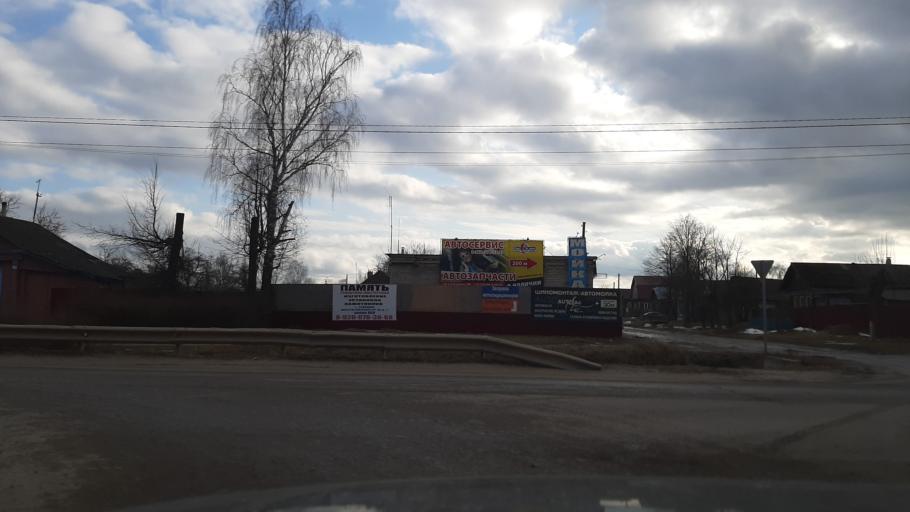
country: RU
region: Ivanovo
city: Teykovo
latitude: 56.8551
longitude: 40.5192
